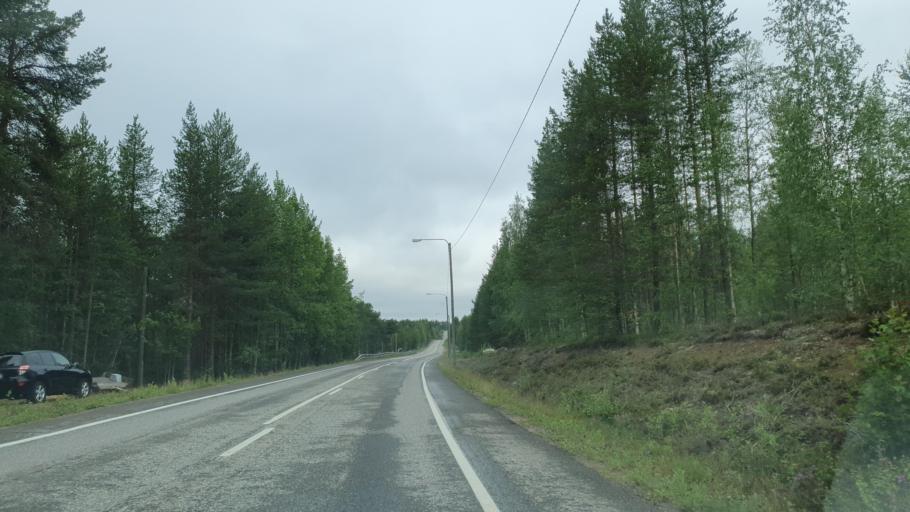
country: FI
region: Lapland
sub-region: Pohjois-Lappi
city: Sodankylae
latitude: 67.3744
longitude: 26.8675
